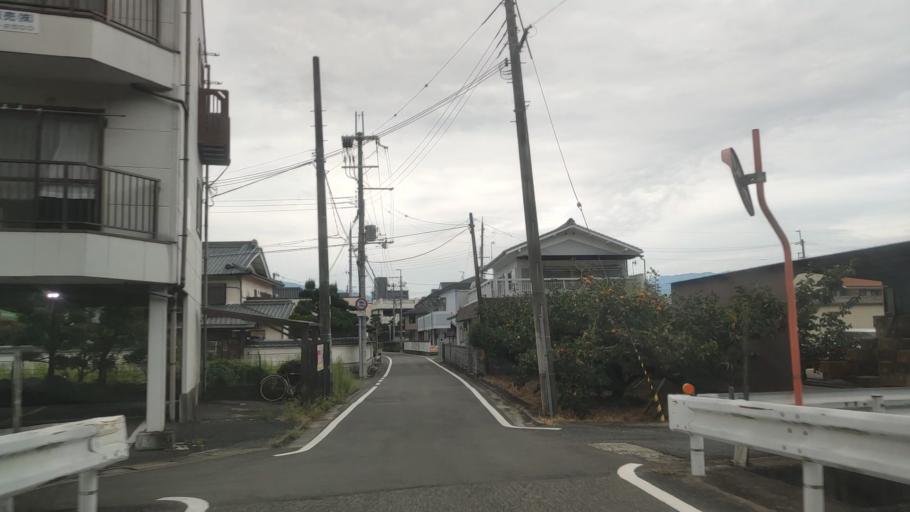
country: JP
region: Wakayama
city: Hashimoto
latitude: 34.3107
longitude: 135.6144
